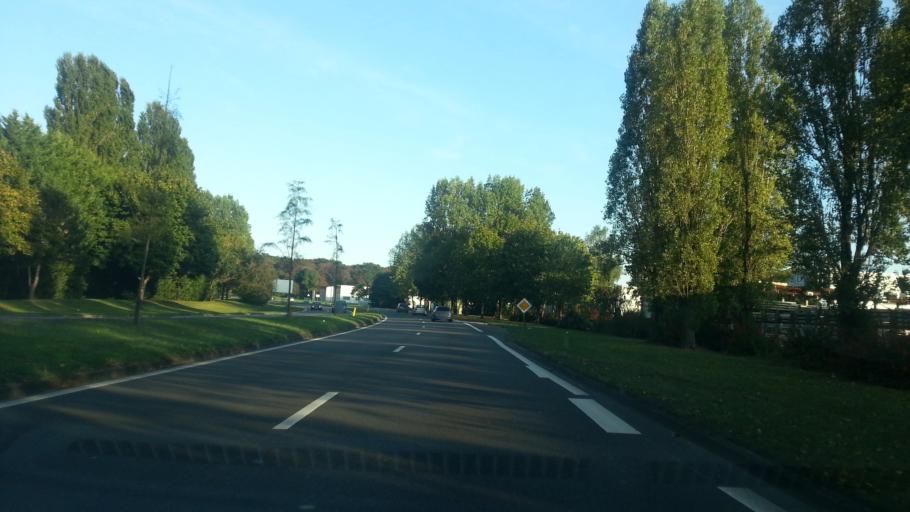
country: FR
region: Picardie
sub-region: Departement de l'Oise
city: Jaux
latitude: 49.3930
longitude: 2.7927
